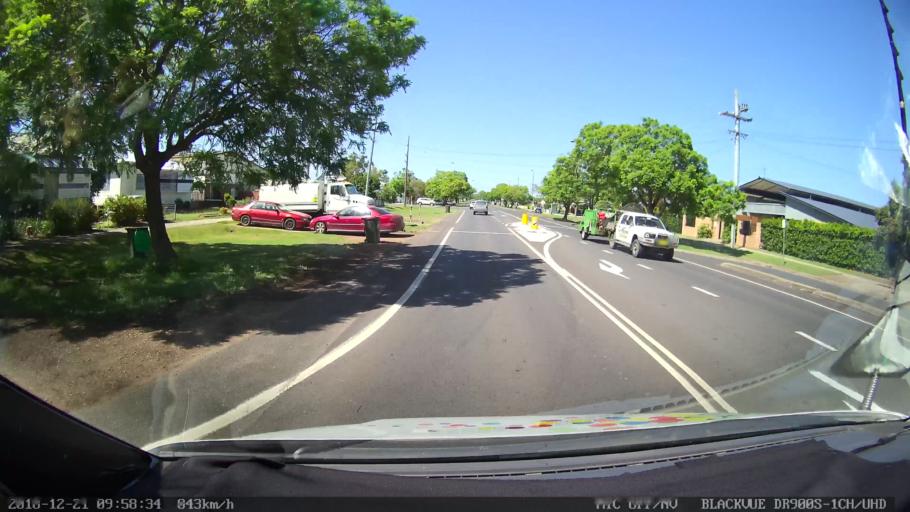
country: AU
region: New South Wales
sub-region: Clarence Valley
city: Grafton
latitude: -29.6733
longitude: 152.9348
